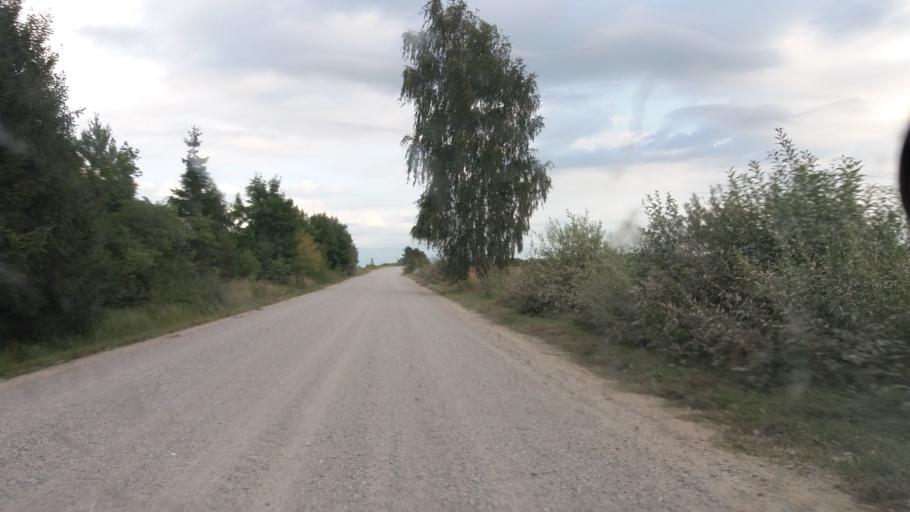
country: LV
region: Talsu Rajons
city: Sabile
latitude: 57.0332
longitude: 22.5749
